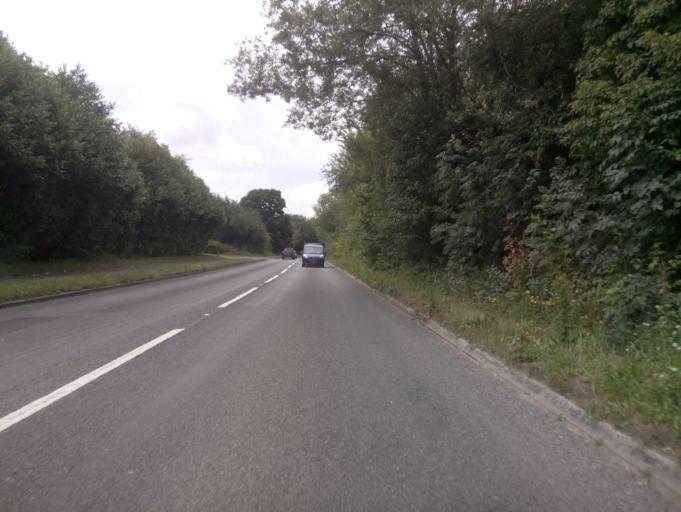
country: GB
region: England
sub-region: Somerset
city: Yeovil
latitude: 50.9184
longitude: -2.6320
